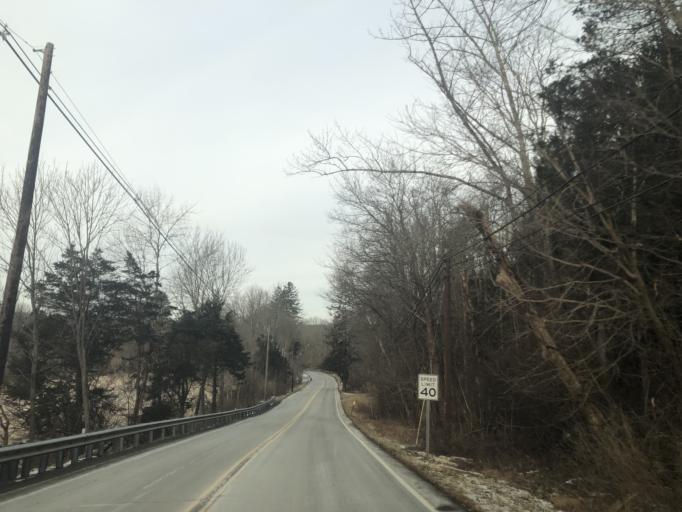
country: US
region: New Jersey
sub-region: Warren County
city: Oxford
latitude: 40.9186
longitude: -74.9862
